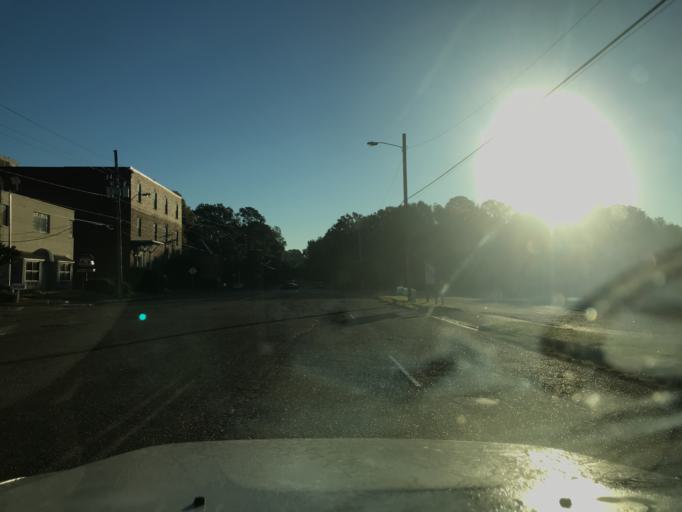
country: US
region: Mississippi
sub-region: Hinds County
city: Jackson
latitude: 32.3501
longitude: -90.1740
